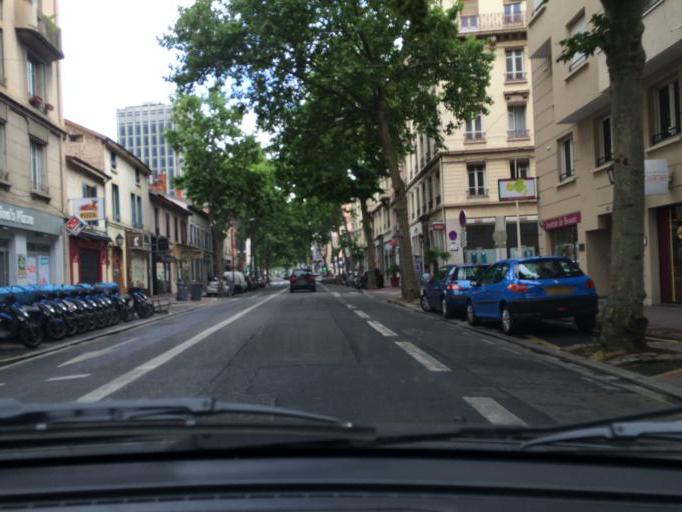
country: FR
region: Rhone-Alpes
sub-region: Departement du Rhone
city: Villeurbanne
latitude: 45.7436
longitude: 4.8728
